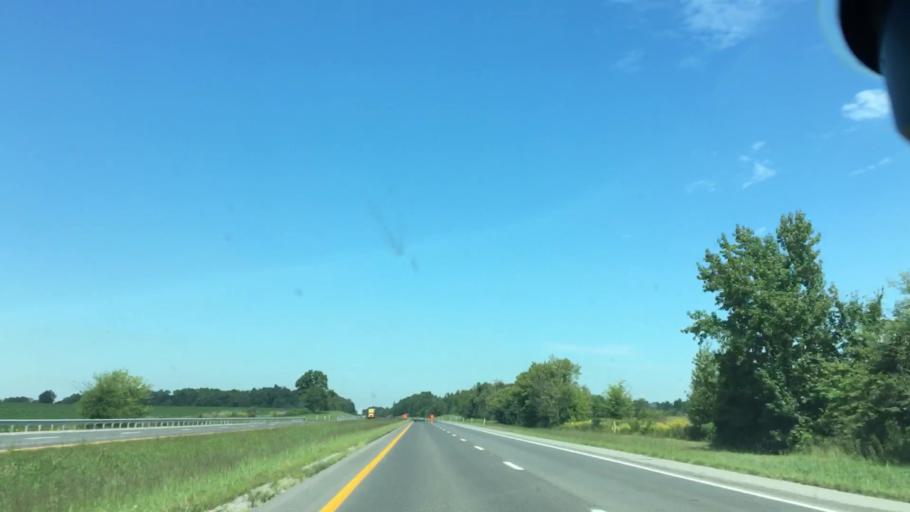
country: US
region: Kentucky
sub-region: Webster County
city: Sebree
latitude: 37.5112
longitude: -87.4748
